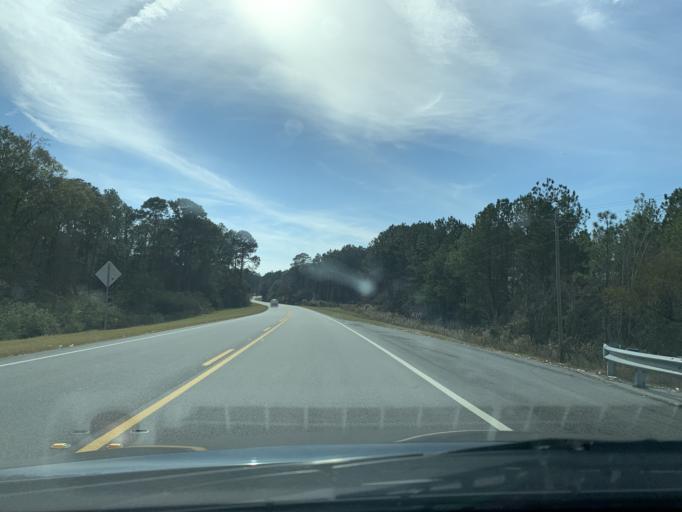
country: US
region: Georgia
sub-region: Turner County
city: Ashburn
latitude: 31.7288
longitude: -83.5808
